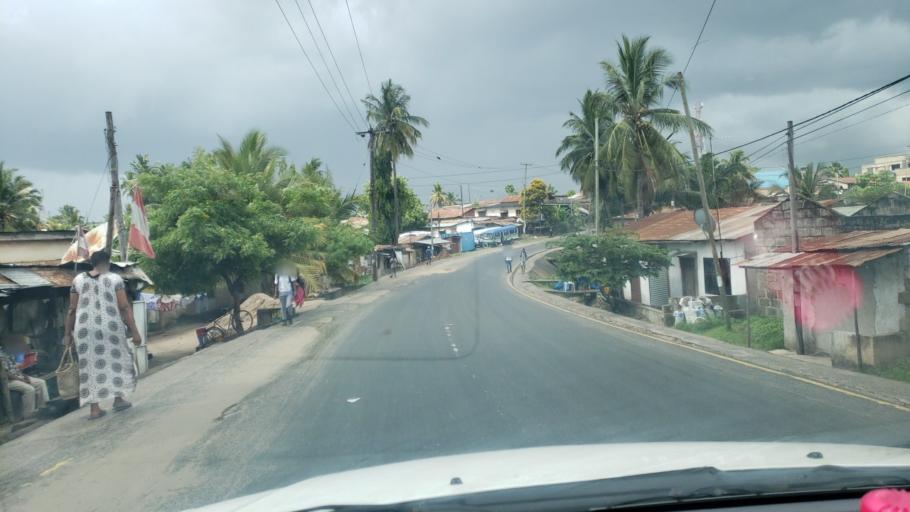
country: TZ
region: Dar es Salaam
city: Magomeni
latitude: -6.8052
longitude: 39.2450
